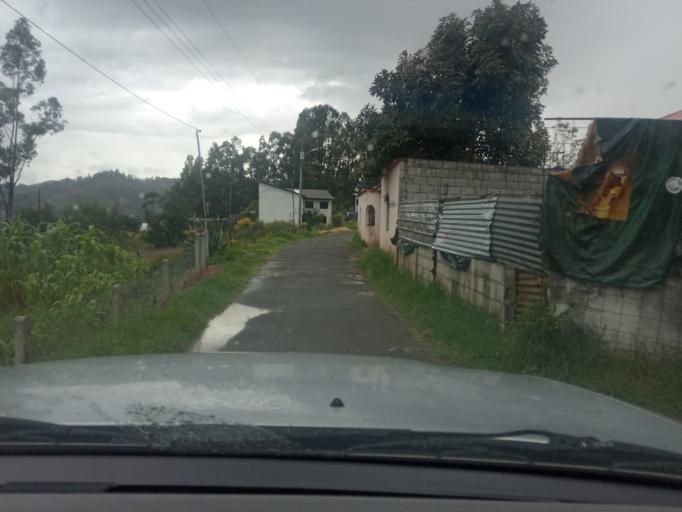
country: EC
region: Azuay
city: Llacao
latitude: -2.8670
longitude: -78.9434
